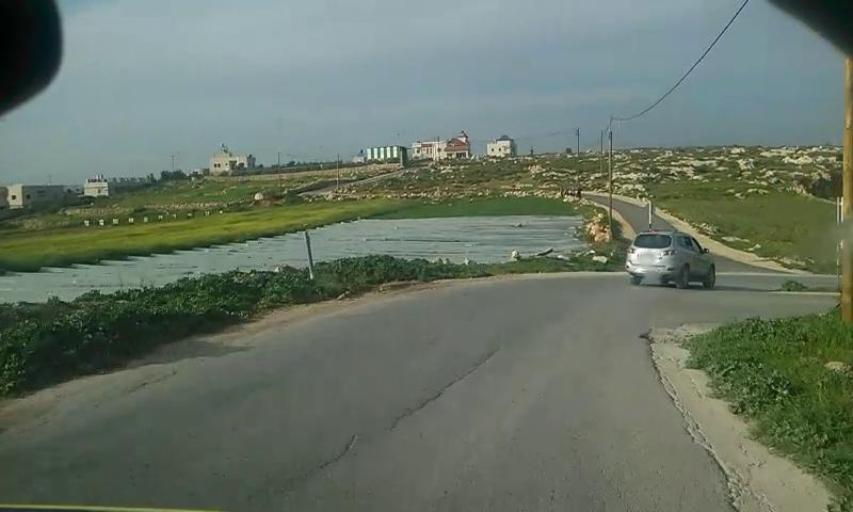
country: PS
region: West Bank
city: Nuba
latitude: 31.6105
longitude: 35.0160
